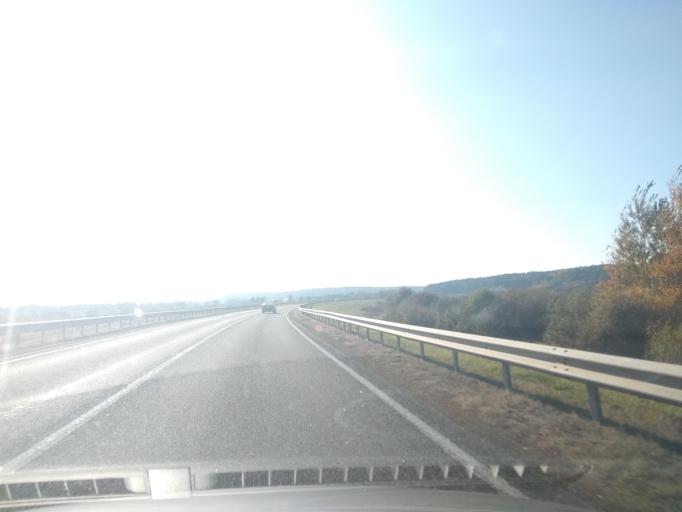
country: BY
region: Grodnenskaya
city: Zhyrovichy
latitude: 53.0498
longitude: 25.3728
